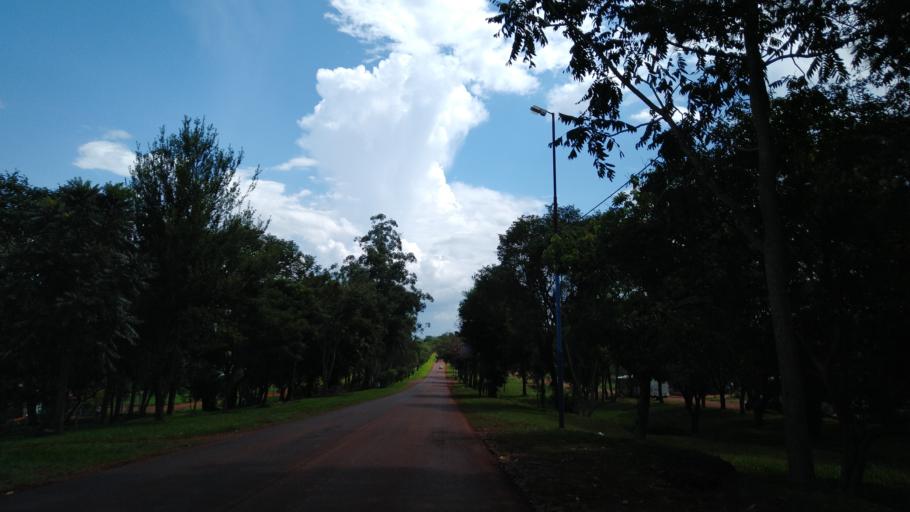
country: AR
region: Misiones
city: Puerto Libertad
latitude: -25.9698
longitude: -54.5620
